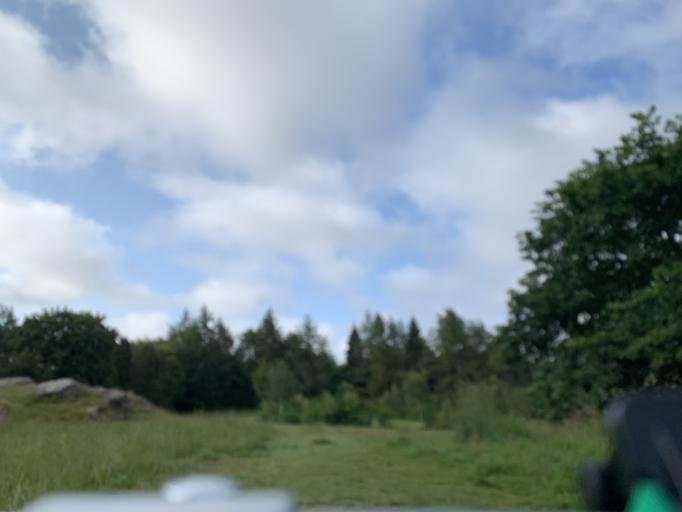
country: GB
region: Scotland
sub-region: East Renfrewshire
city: Giffnock
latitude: 55.7931
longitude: -4.3176
